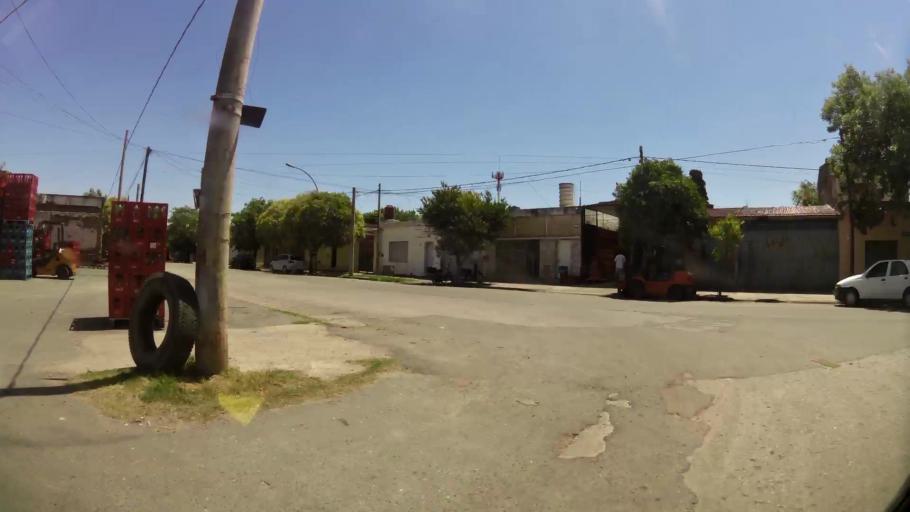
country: AR
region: Cordoba
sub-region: Departamento de Capital
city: Cordoba
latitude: -31.3852
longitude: -64.1479
